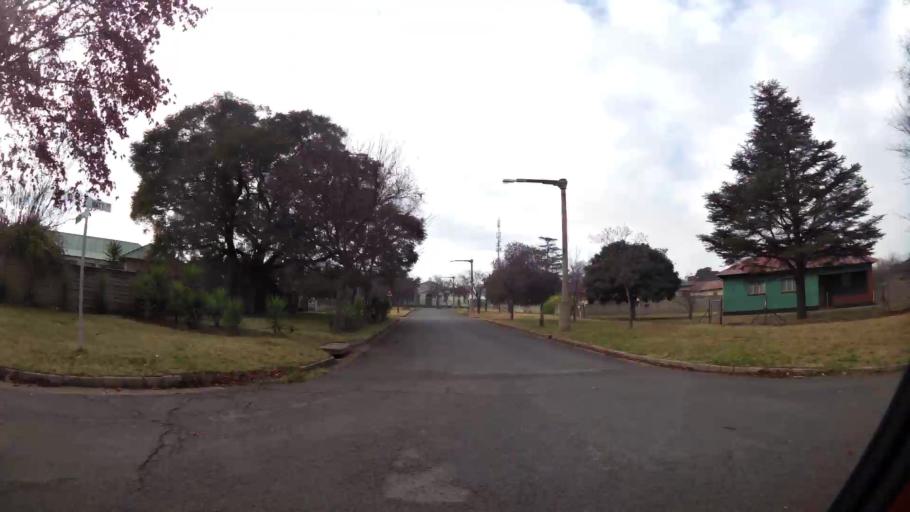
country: ZA
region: Gauteng
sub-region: Sedibeng District Municipality
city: Vanderbijlpark
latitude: -26.6859
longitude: 27.8158
